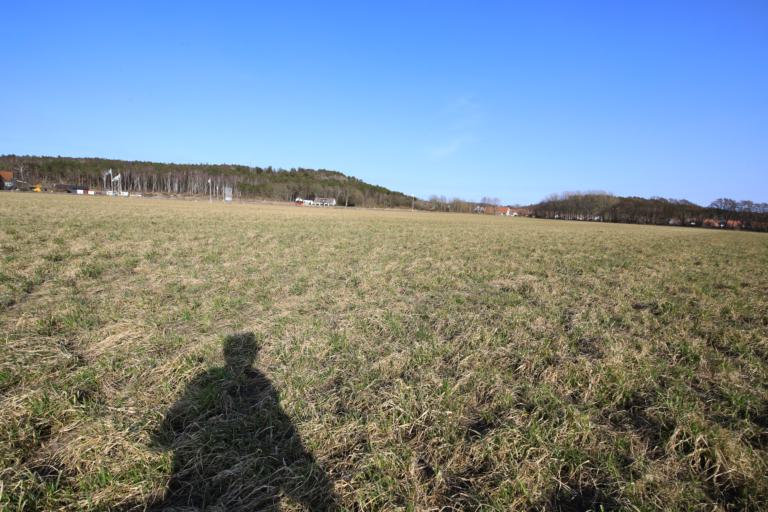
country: SE
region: Halland
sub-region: Varbergs Kommun
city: Varberg
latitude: 57.1419
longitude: 12.2774
